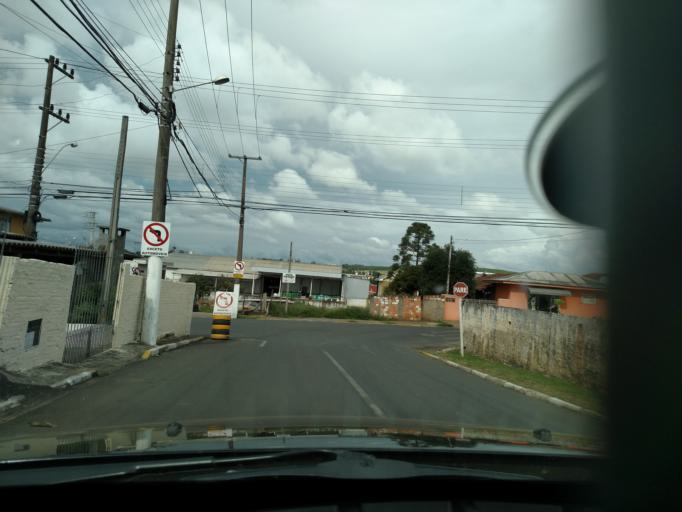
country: BR
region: Santa Catarina
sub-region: Lages
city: Lages
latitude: -27.7985
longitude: -50.3025
